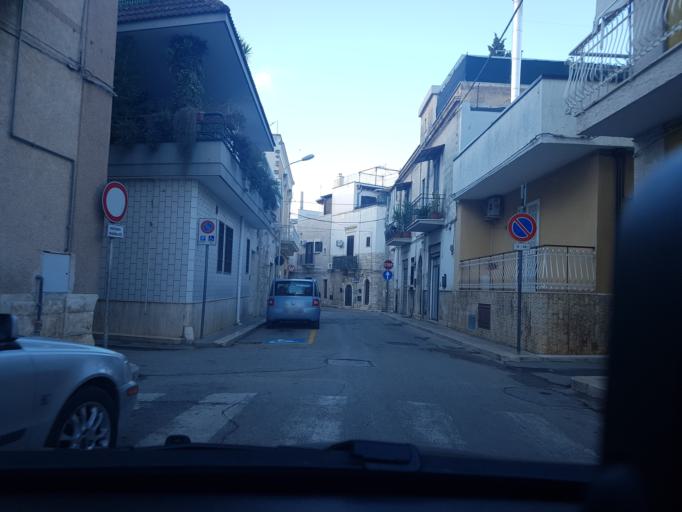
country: IT
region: Apulia
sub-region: Provincia di Bari
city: Bitritto
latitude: 41.0400
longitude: 16.8282
